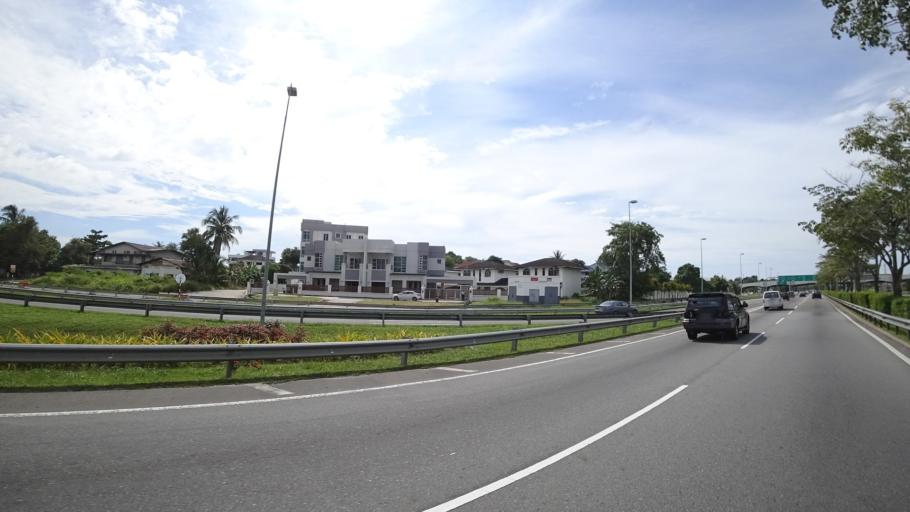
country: BN
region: Brunei and Muara
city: Bandar Seri Begawan
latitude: 4.9121
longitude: 114.9212
